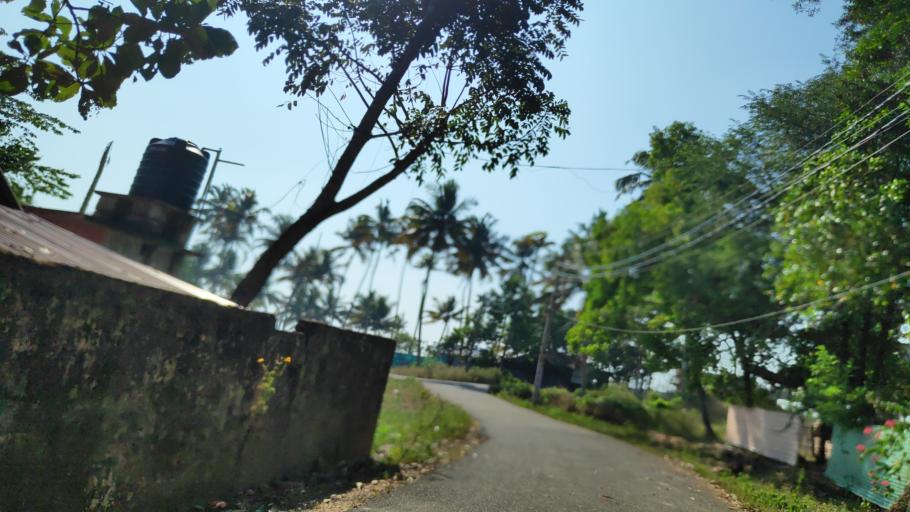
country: IN
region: Kerala
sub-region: Alappuzha
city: Alleppey
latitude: 9.5330
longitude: 76.3105
